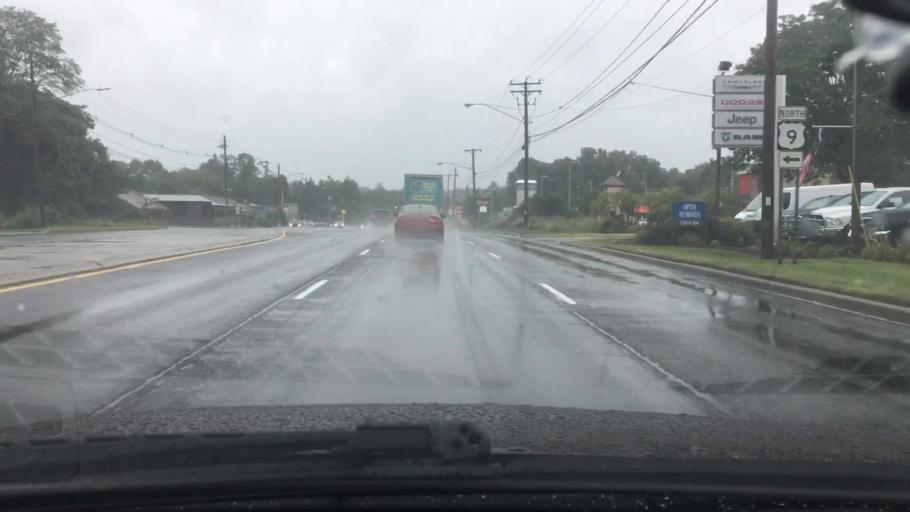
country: US
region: New York
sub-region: Dutchess County
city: Spackenkill
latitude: 41.6455
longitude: -73.9235
